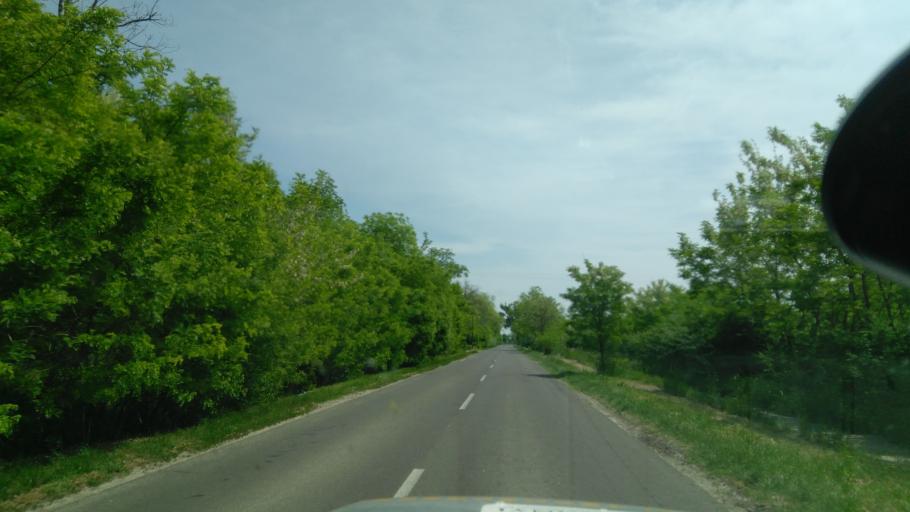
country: HU
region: Csongrad
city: Szekkutas
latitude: 46.5755
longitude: 20.4577
